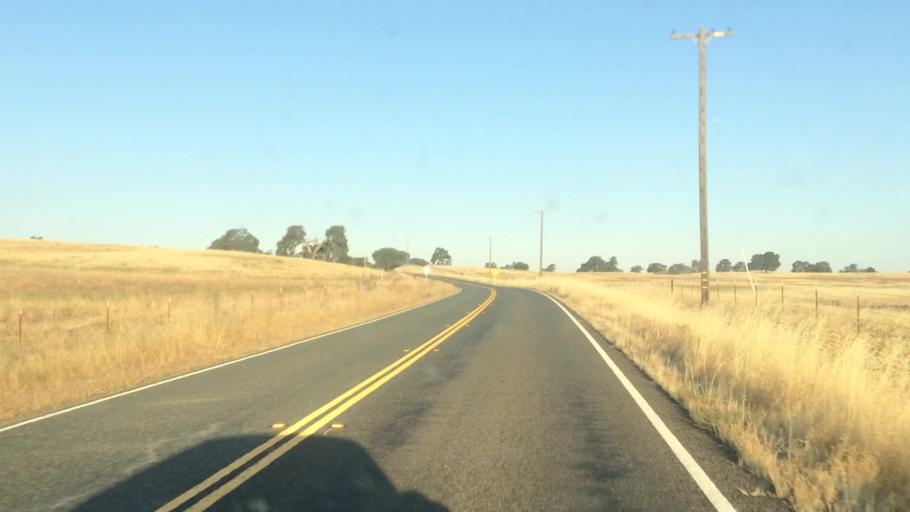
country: US
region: California
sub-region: Amador County
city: Ione
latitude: 38.3617
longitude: -121.0413
